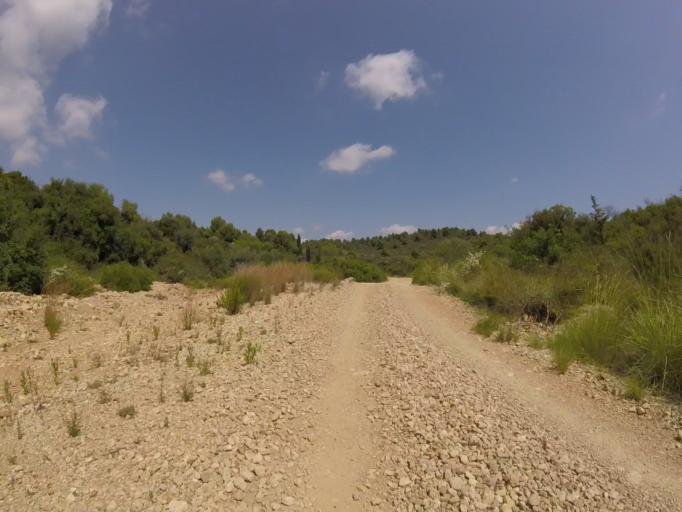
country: ES
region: Valencia
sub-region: Provincia de Castello
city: Torreblanca
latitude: 40.2114
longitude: 0.1394
